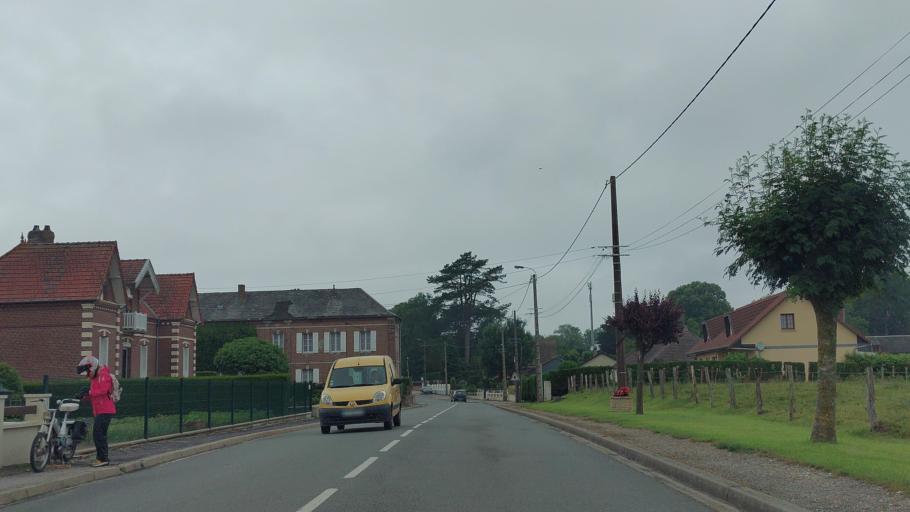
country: FR
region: Picardie
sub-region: Departement de la Somme
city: Bethencourt-sur-Mer
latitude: 50.0876
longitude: 1.4851
